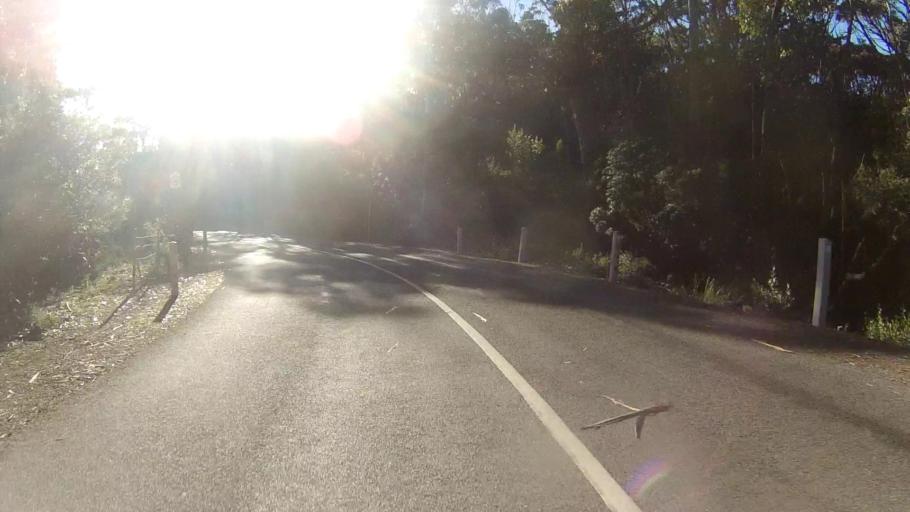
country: AU
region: Tasmania
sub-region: Clarence
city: Sandford
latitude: -43.0363
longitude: 147.9478
